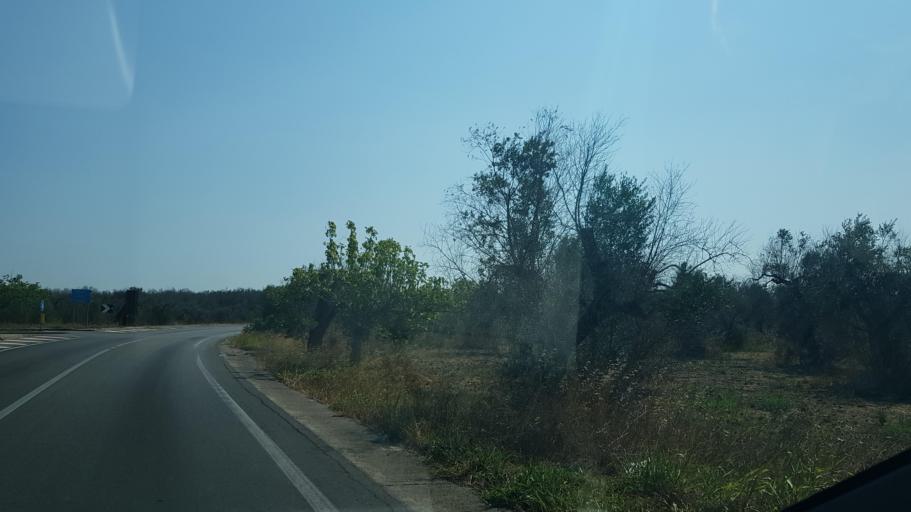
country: IT
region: Apulia
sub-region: Provincia di Lecce
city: Ruffano
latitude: 40.0020
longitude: 18.2808
